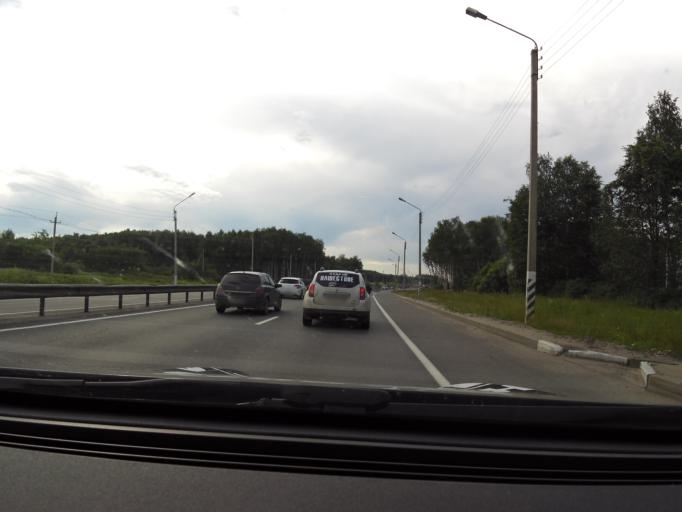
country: RU
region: Vladimir
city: Vyazniki
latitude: 56.2231
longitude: 42.1327
